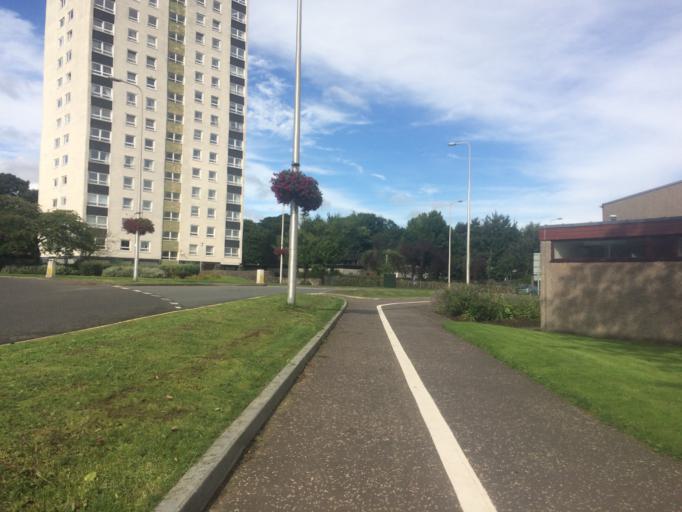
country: GB
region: Scotland
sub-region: Fife
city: Glenrothes
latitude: 56.1950
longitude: -3.1787
